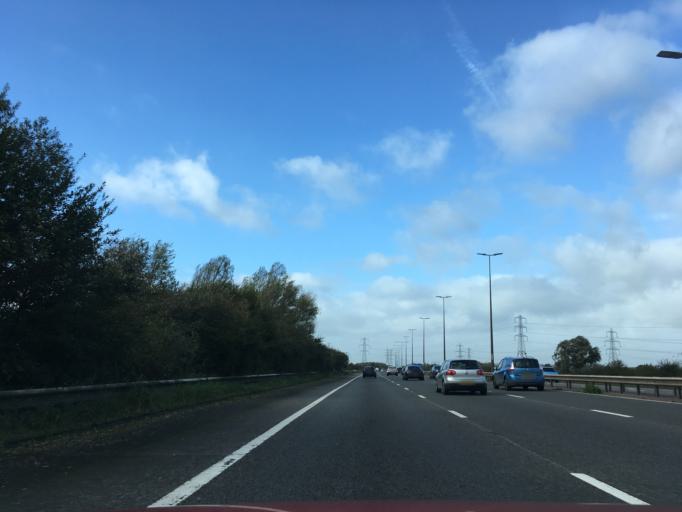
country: GB
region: Wales
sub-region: Monmouthshire
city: Caldicot
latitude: 51.5808
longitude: -2.7583
